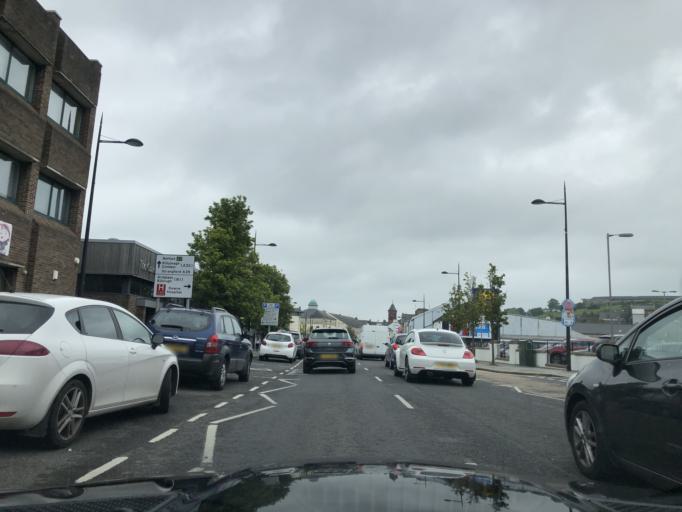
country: GB
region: Northern Ireland
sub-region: Down District
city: Downpatrick
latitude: 54.3259
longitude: -5.7189
